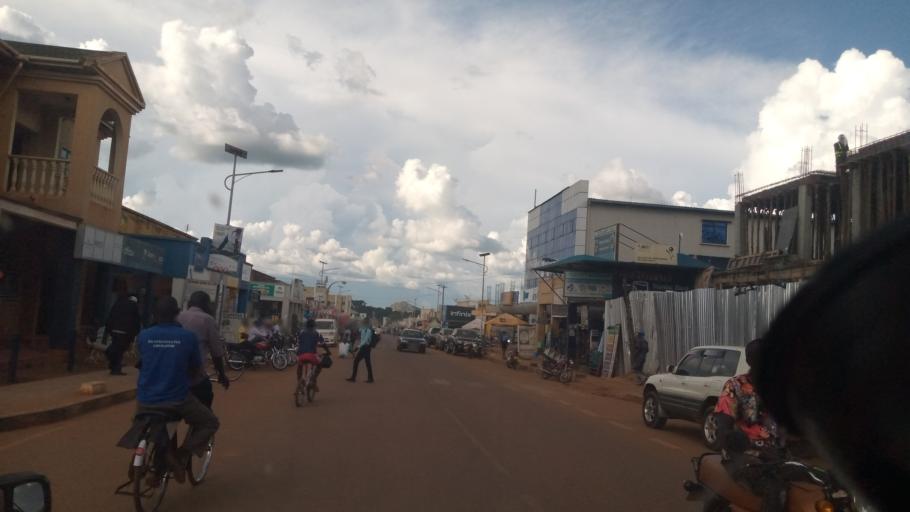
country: UG
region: Northern Region
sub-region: Lira District
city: Lira
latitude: 2.2395
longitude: 32.8948
